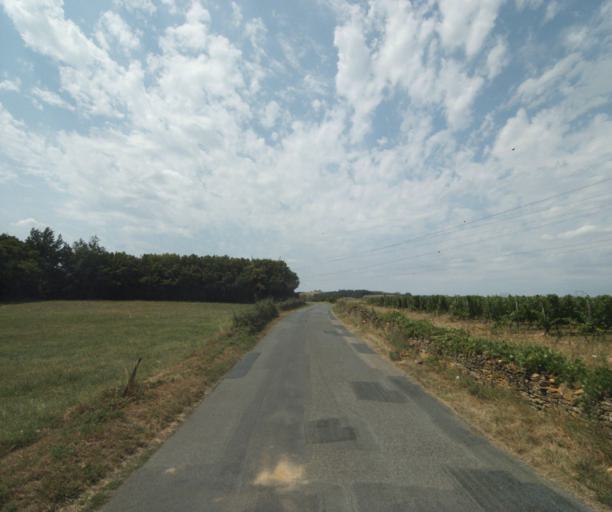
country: FR
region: Rhone-Alpes
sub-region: Departement du Rhone
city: Saint-Germain-Nuelles
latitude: 45.8676
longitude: 4.6062
